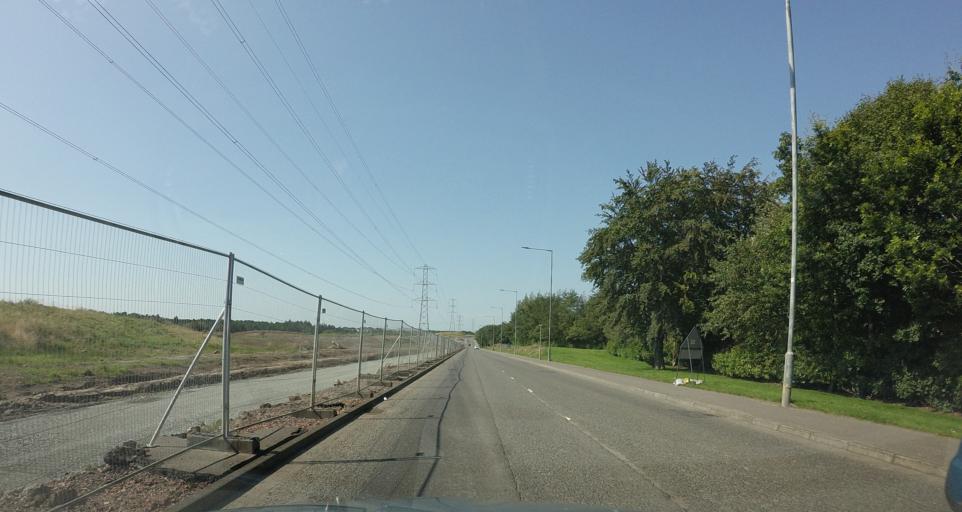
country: GB
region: Scotland
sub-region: South Lanarkshire
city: East Kilbride
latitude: 55.7417
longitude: -4.1738
